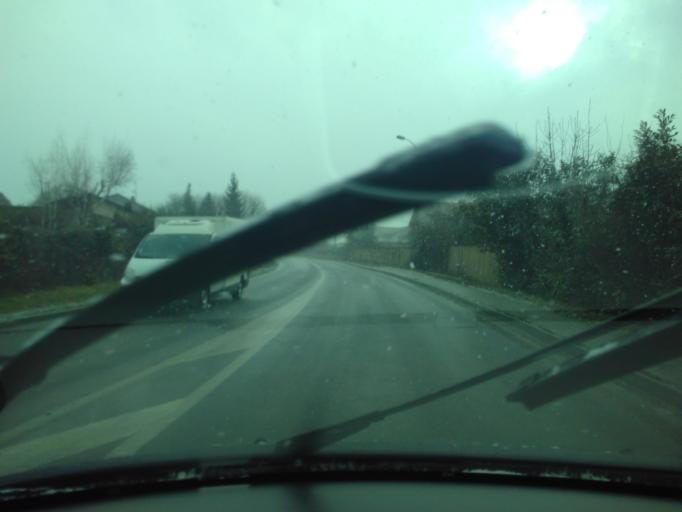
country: FR
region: Rhone-Alpes
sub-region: Departement de la Haute-Savoie
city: Saint-Julien-en-Genevois
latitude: 46.1350
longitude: 6.0796
